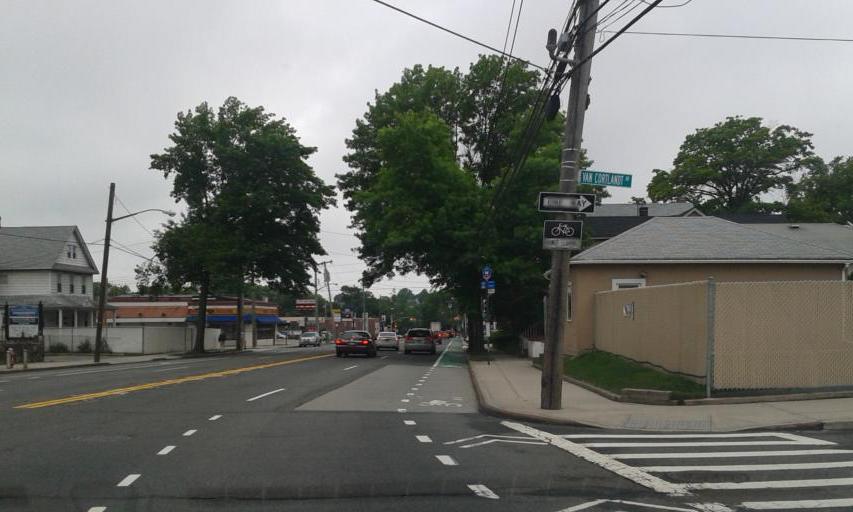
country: US
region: New Jersey
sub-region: Hudson County
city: Bayonne
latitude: 40.6144
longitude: -74.1017
